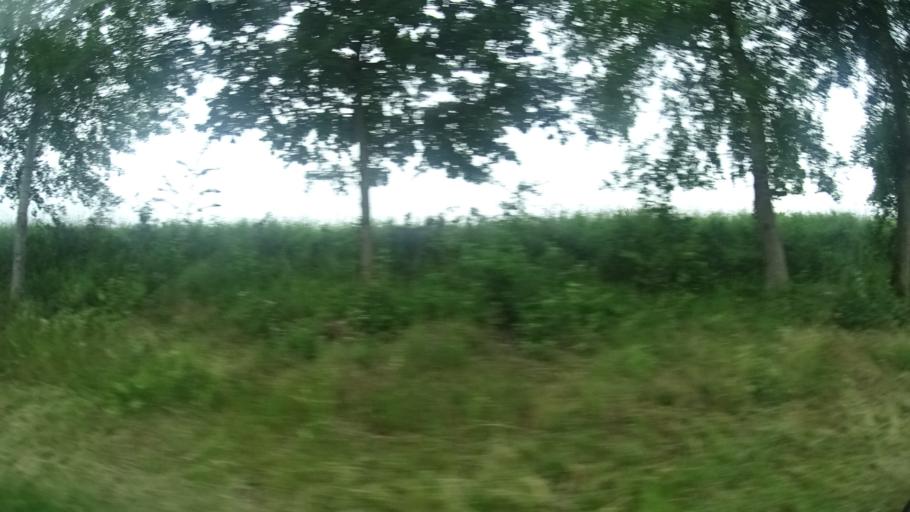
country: DE
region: Bavaria
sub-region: Regierungsbezirk Unterfranken
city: Schollkrippen
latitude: 50.0851
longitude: 9.2357
